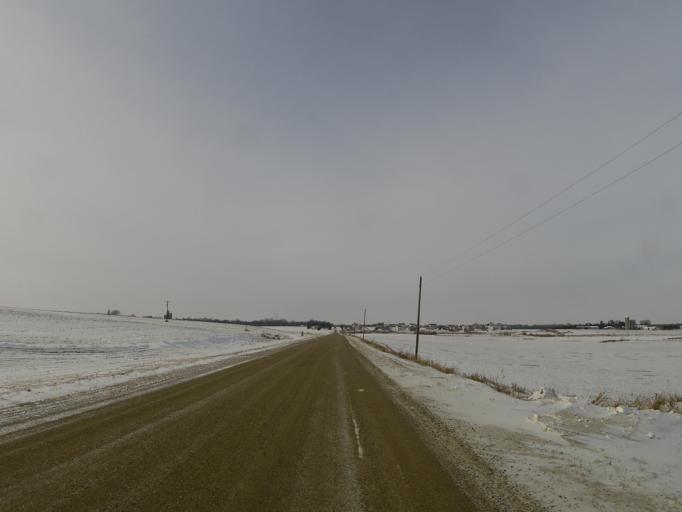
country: US
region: Minnesota
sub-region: Carver County
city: Mayer
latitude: 44.8912
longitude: -93.8619
